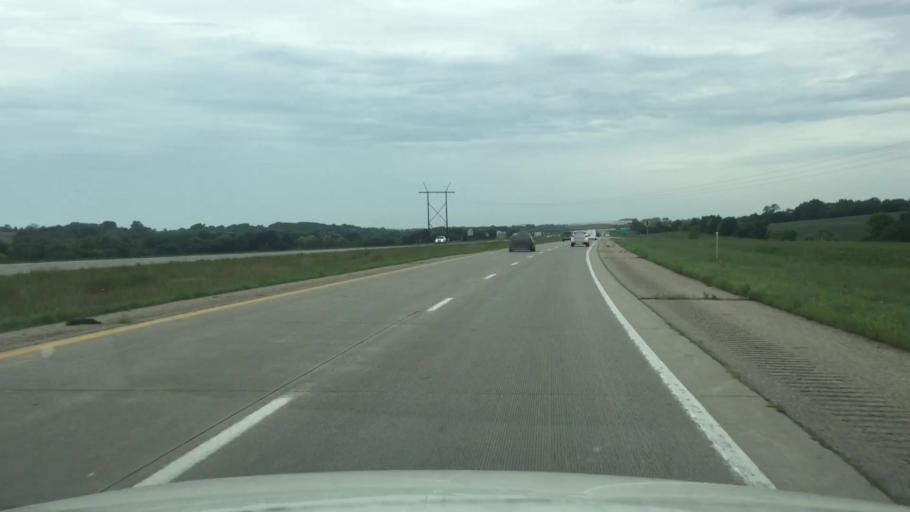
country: US
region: Iowa
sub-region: Warren County
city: Norwalk
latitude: 41.4997
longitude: -93.6279
